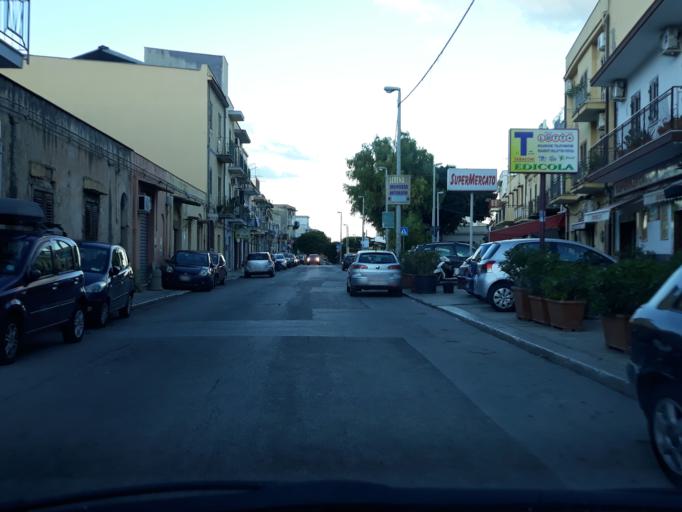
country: IT
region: Sicily
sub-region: Palermo
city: Villa Ciambra
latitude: 38.0900
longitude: 13.3306
